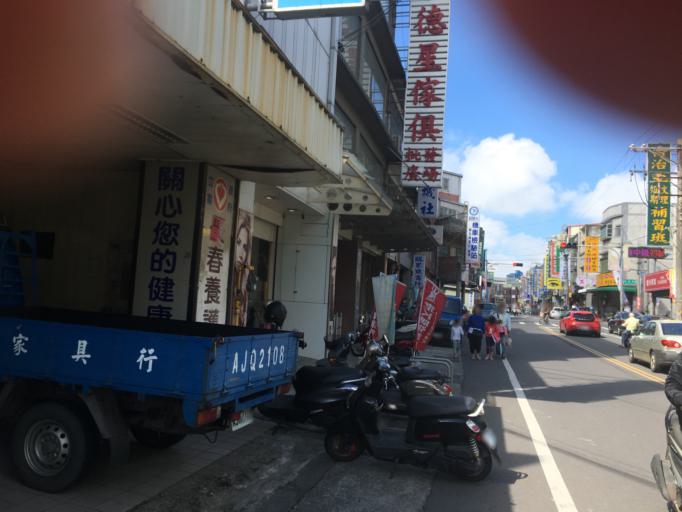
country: TW
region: Taiwan
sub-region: Hsinchu
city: Zhubei
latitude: 24.8994
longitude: 121.0474
